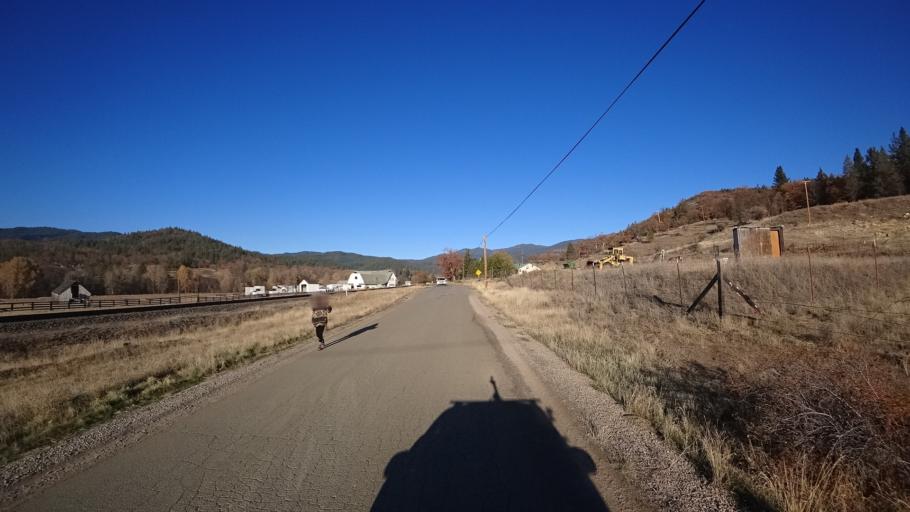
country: US
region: Oregon
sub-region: Jackson County
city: Ashland
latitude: 42.0012
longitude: -122.6384
